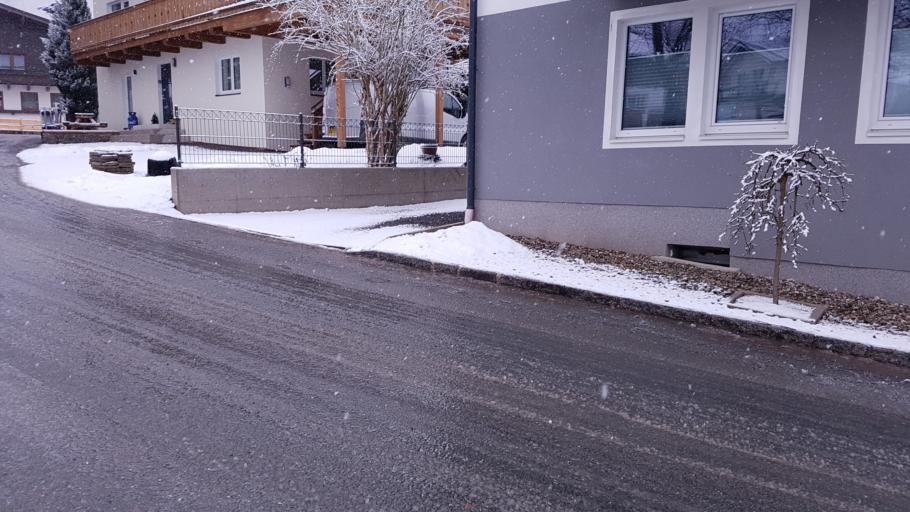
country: AT
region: Salzburg
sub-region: Politischer Bezirk Zell am See
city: Neukirchen am Grossvenediger
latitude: 47.2517
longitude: 12.2736
